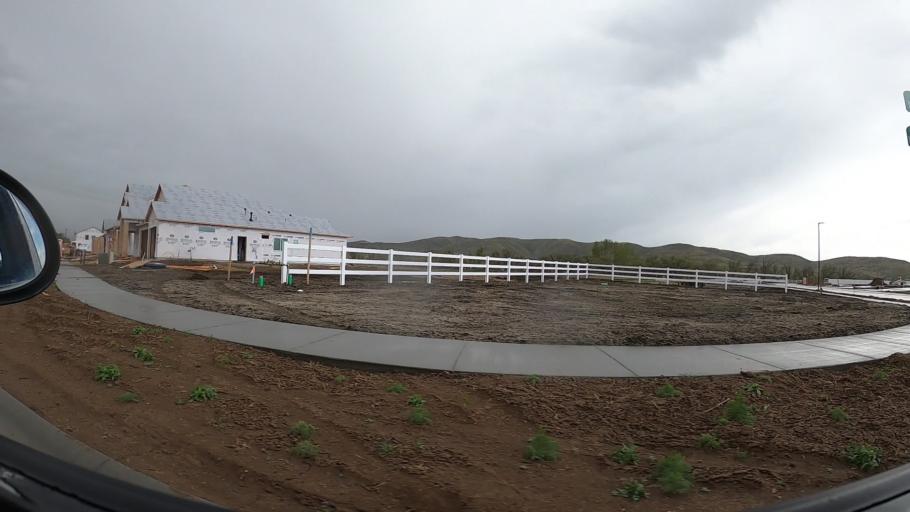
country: US
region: Idaho
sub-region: Ada County
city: Eagle
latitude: 43.7340
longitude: -116.2822
